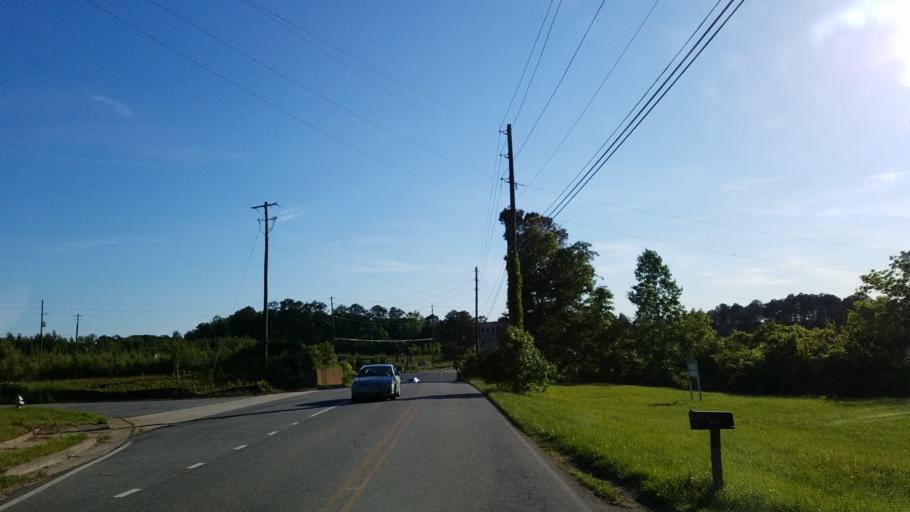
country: US
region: Georgia
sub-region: Cherokee County
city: Holly Springs
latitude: 34.1739
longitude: -84.5472
